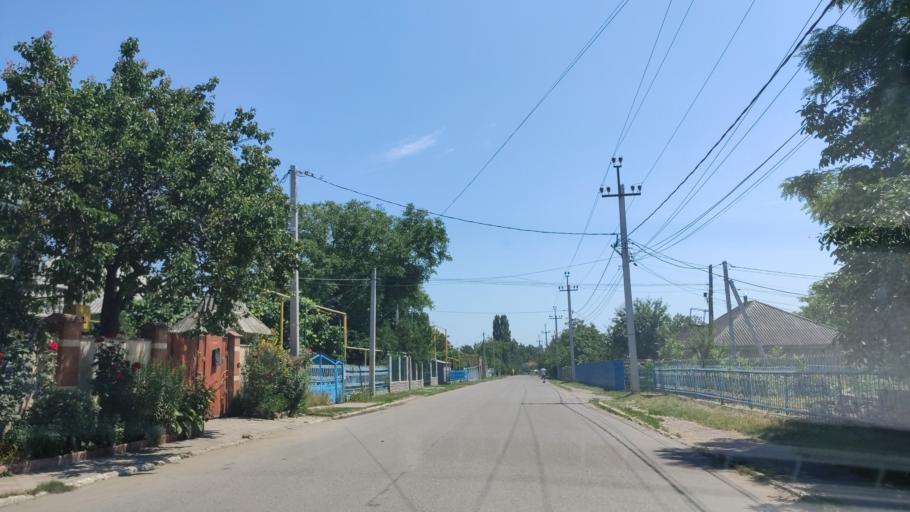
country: MD
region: Raionul Soroca
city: Soroca
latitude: 48.1466
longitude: 28.2854
